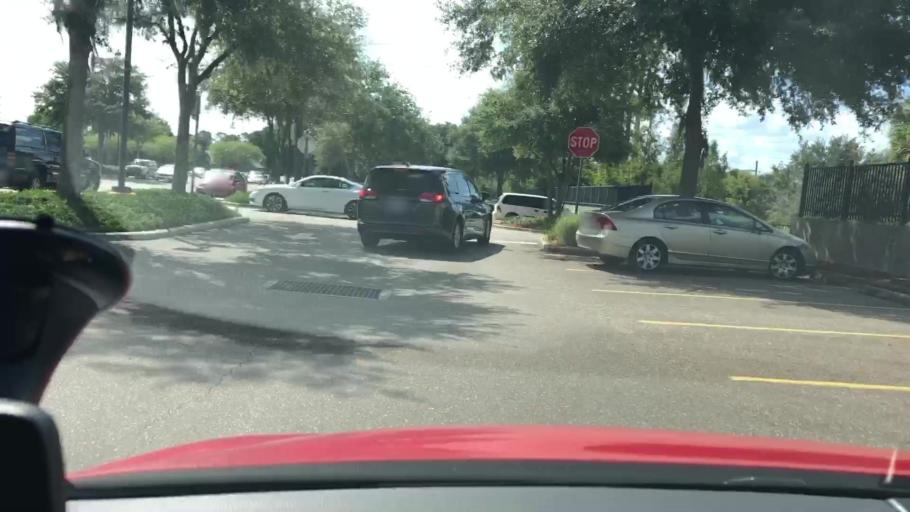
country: US
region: Florida
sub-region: Volusia County
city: Deltona
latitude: 28.9136
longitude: -81.2807
